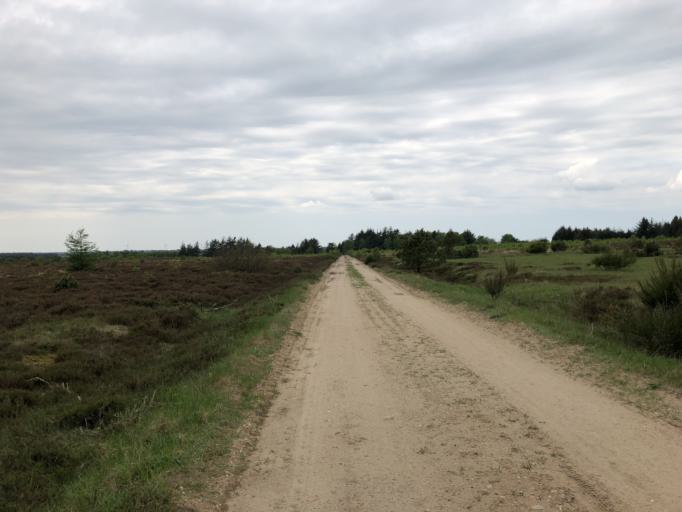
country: DK
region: Central Jutland
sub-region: Holstebro Kommune
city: Ulfborg
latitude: 56.2983
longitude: 8.4139
